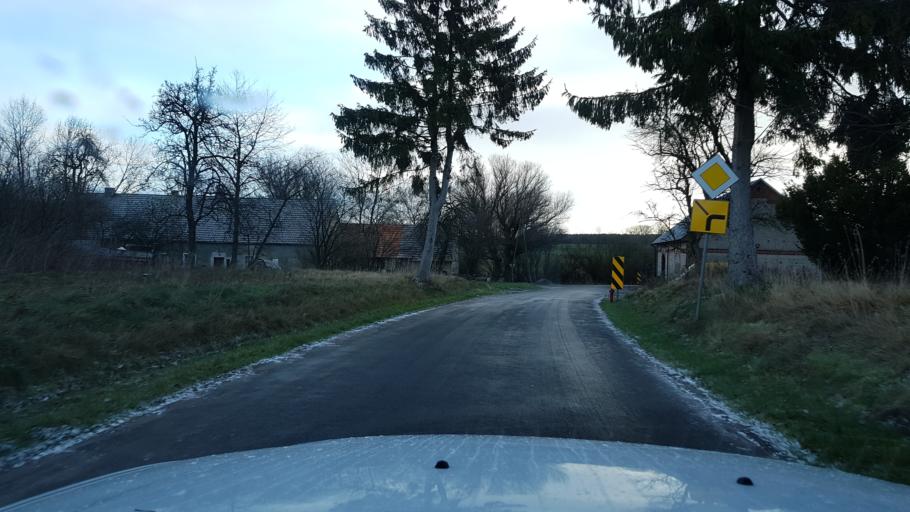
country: PL
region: West Pomeranian Voivodeship
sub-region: Powiat gryficki
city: Brojce
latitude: 54.0351
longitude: 15.3604
